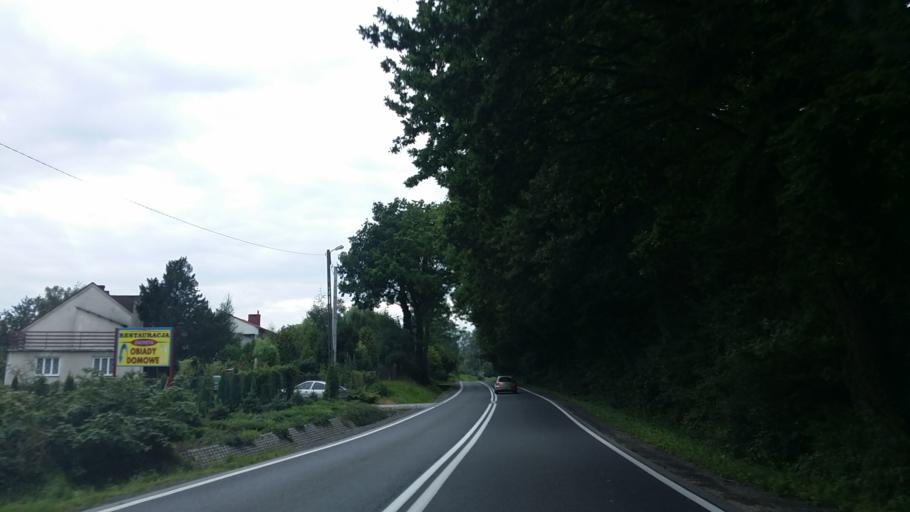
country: PL
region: Lesser Poland Voivodeship
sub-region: Powiat wadowicki
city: Brzeznica
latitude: 49.9641
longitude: 19.6057
